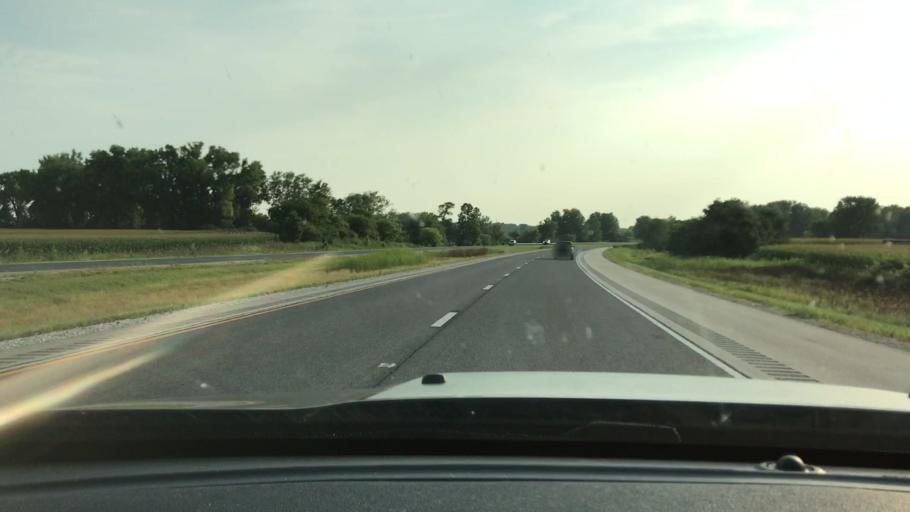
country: US
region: Illinois
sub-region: Henry County
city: Kewanee
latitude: 41.4073
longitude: -89.9711
